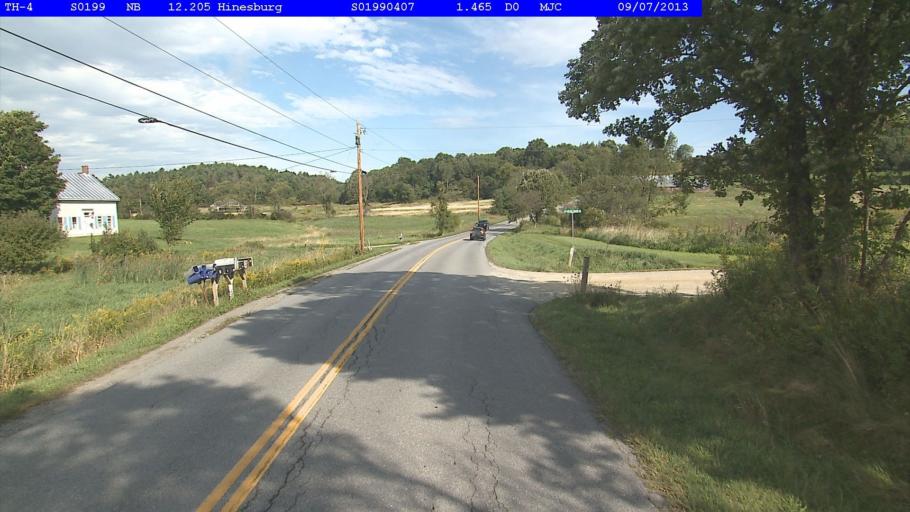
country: US
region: Vermont
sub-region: Chittenden County
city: Hinesburg
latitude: 44.2990
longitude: -73.1092
